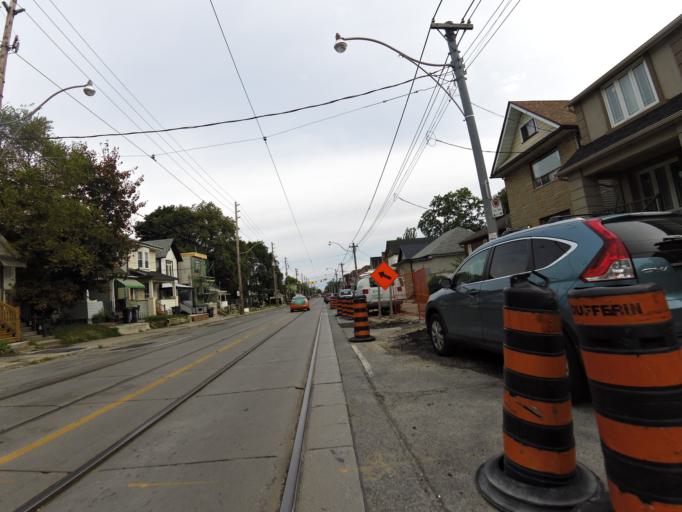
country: CA
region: Ontario
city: Toronto
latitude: 43.6714
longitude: -79.3187
